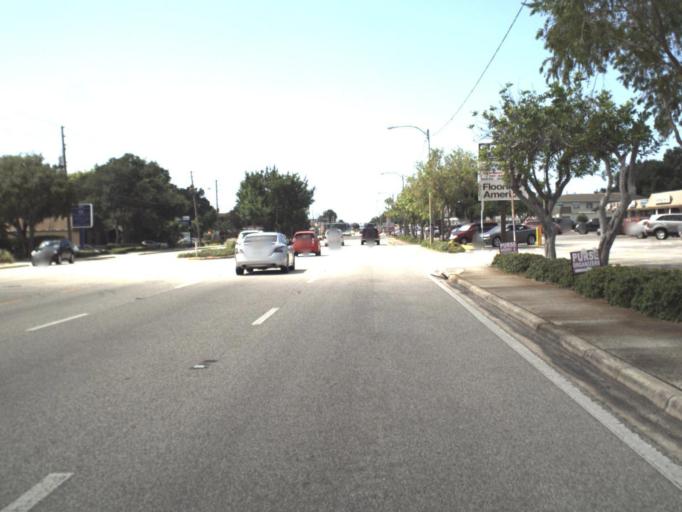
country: US
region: Florida
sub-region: Pinellas County
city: Seminole
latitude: 27.8560
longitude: -82.7872
